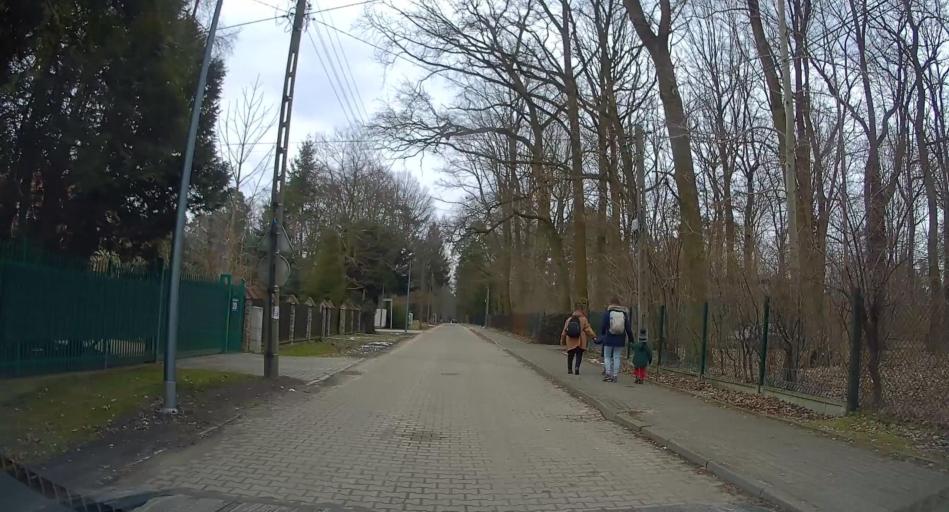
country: PL
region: Masovian Voivodeship
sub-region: Powiat piaseczynski
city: Piaseczno
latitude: 52.0583
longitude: 21.0019
